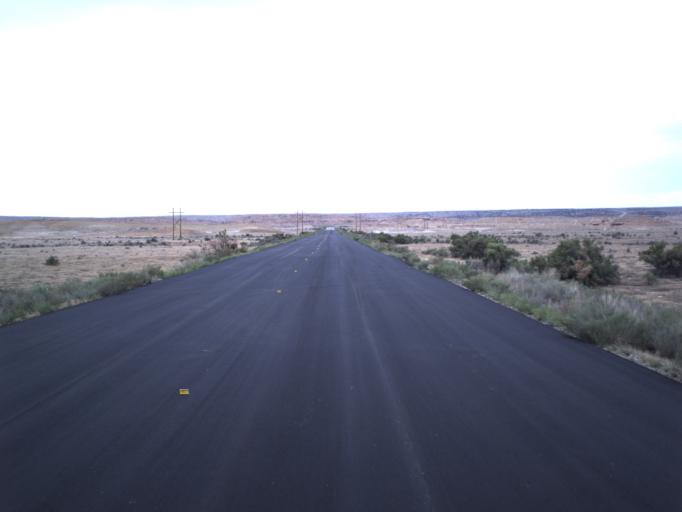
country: US
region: Utah
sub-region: Uintah County
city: Naples
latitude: 40.1139
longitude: -109.2400
